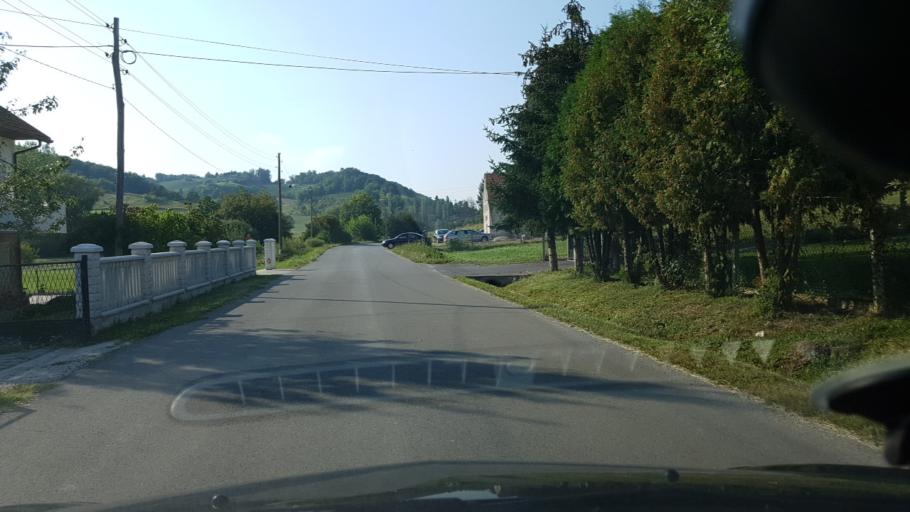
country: HR
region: Krapinsko-Zagorska
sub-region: Grad Krapina
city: Krapina
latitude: 46.1124
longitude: 15.8660
